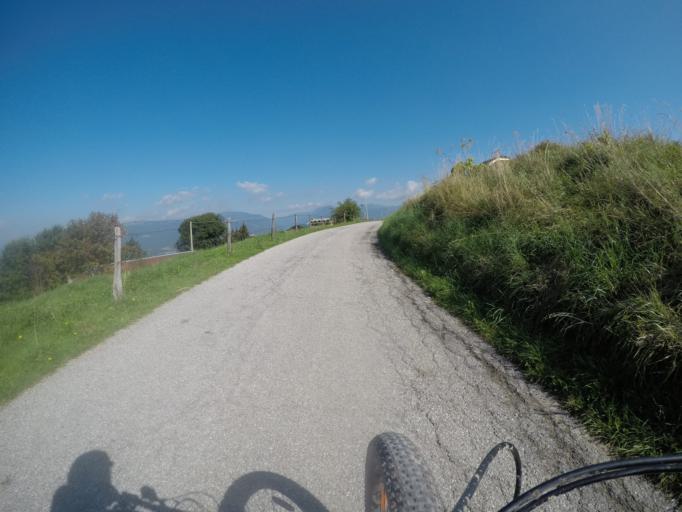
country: IT
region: Veneto
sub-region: Provincia di Vicenza
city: Canove di Roana
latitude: 45.8435
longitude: 11.4980
